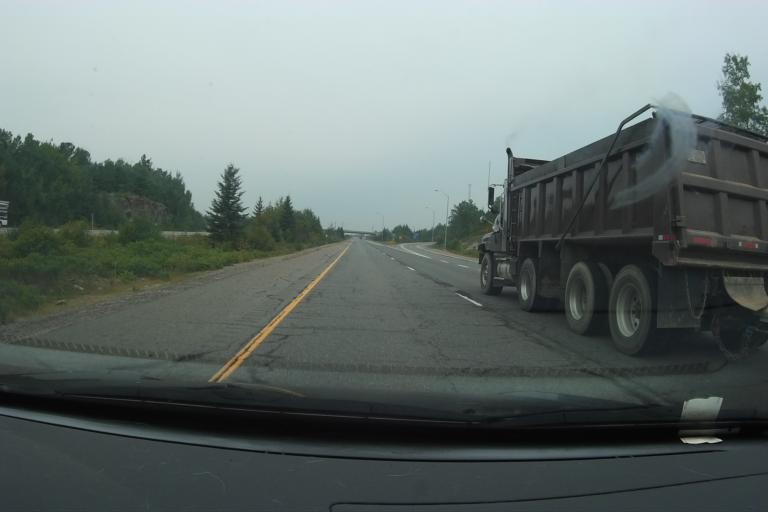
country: CA
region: Ontario
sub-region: Nipissing District
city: North Bay
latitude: 46.2619
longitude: -79.3869
